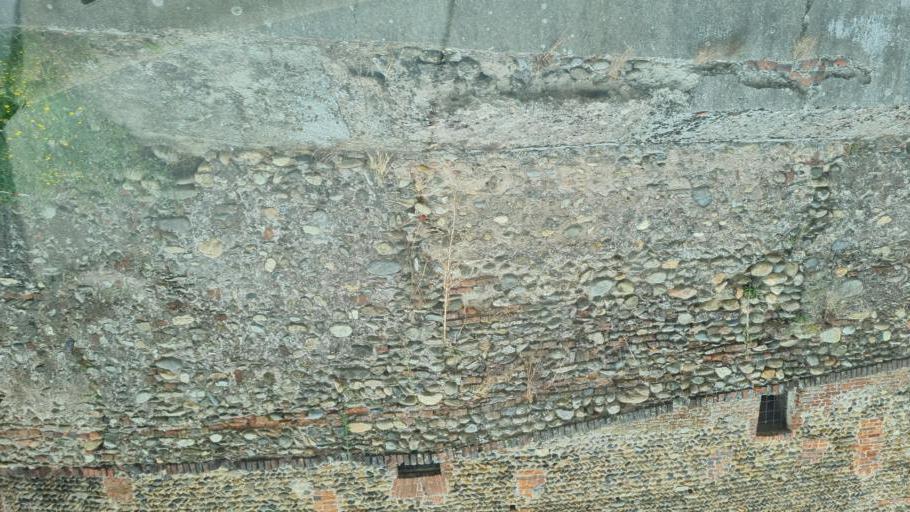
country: IT
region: Piedmont
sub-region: Provincia di Vercelli
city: Rovasenda
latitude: 45.5355
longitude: 8.3129
